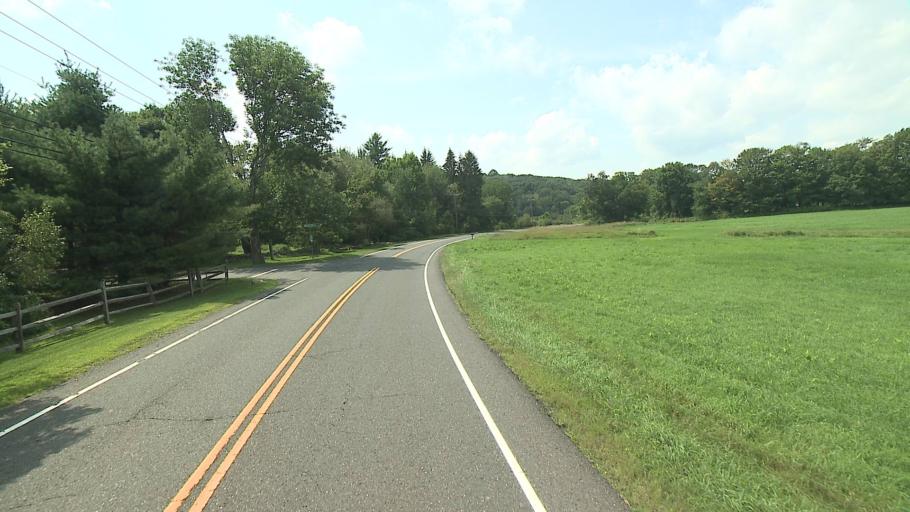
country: US
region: Connecticut
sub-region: Litchfield County
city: New Preston
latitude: 41.6354
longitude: -73.3380
